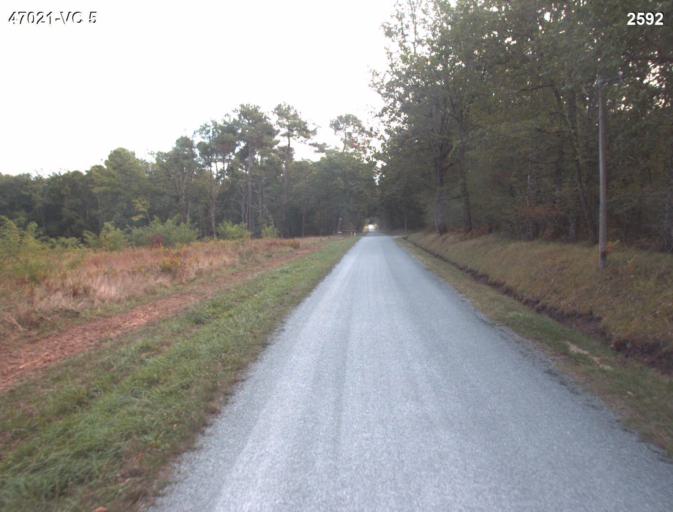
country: FR
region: Aquitaine
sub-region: Departement du Lot-et-Garonne
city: Barbaste
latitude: 44.1438
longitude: 0.2663
